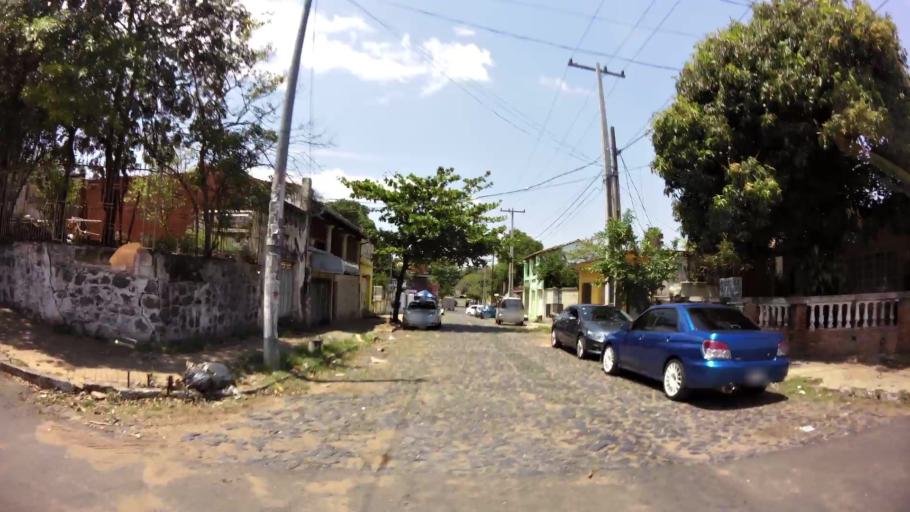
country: PY
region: Asuncion
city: Asuncion
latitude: -25.3008
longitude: -57.6478
